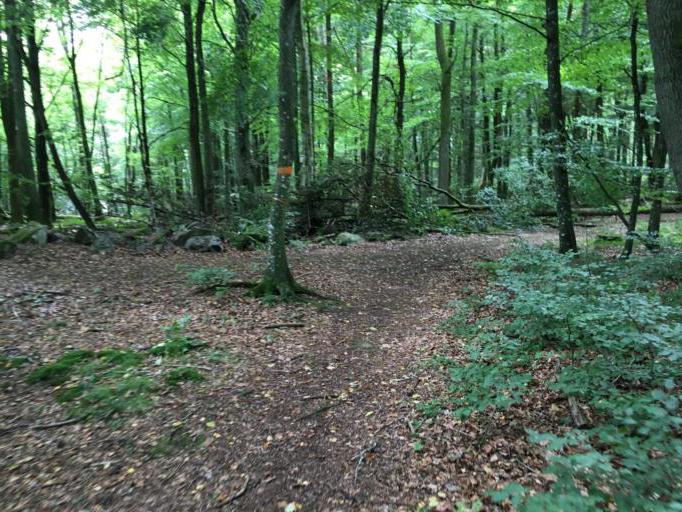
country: SE
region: Skane
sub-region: Eslovs Kommun
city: Stehag
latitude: 55.9907
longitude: 13.4250
